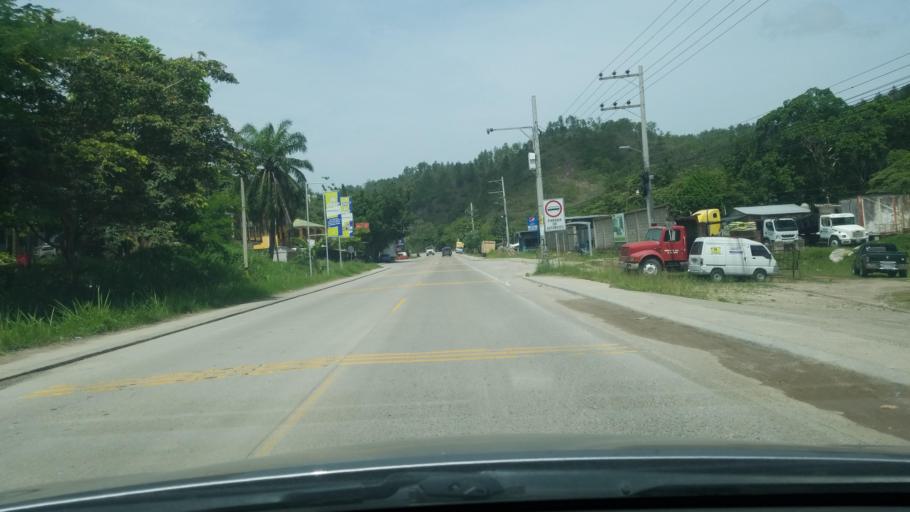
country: HN
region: Copan
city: La Entrada
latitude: 15.0484
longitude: -88.7587
